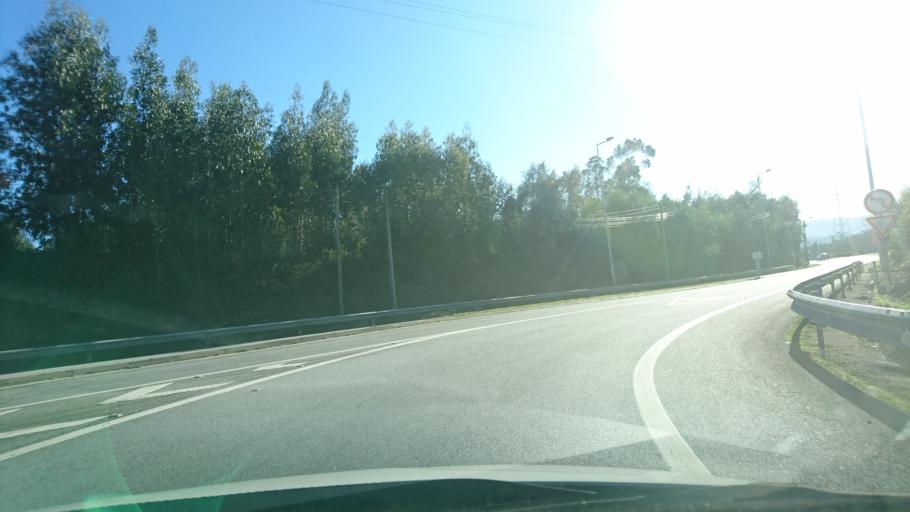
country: PT
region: Porto
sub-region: Paredes
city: Baltar
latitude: 41.1723
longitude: -8.3872
